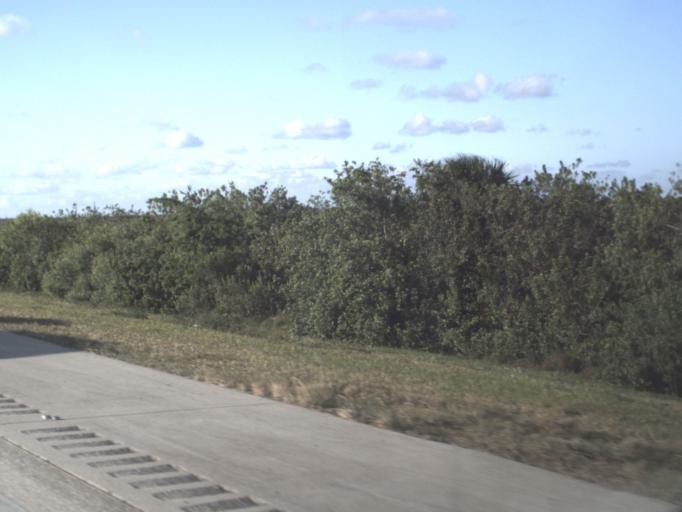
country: US
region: Florida
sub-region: Brevard County
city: Cocoa West
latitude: 28.3116
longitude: -80.7628
